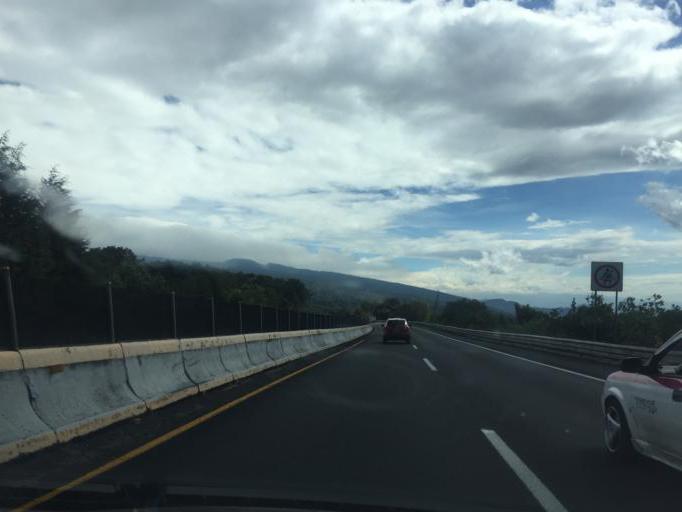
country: MX
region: Morelos
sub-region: Cuernavaca
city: Villa Santiago
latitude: 19.0246
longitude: -99.1909
